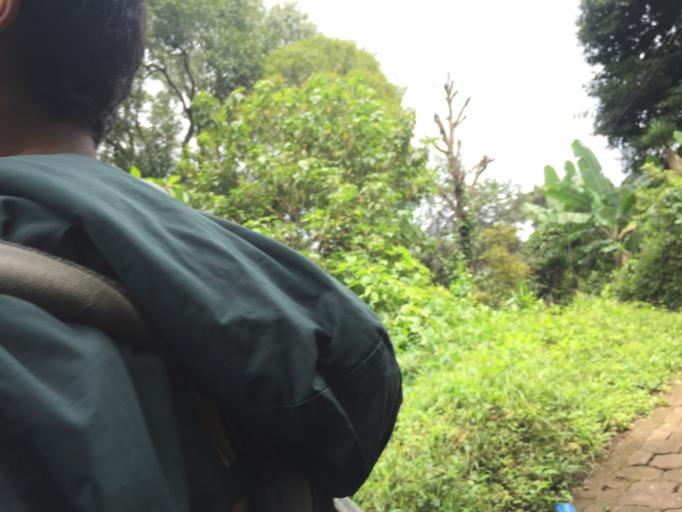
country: GT
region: Guatemala
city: Villa Canales
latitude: 14.4801
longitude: -90.5242
